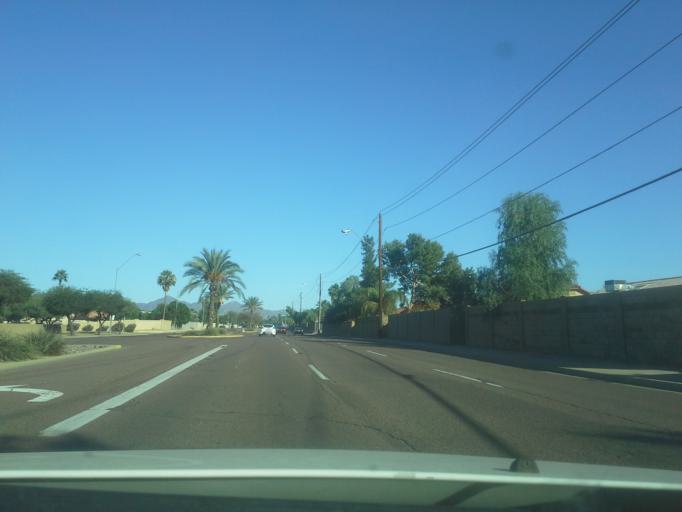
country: US
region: Arizona
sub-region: Maricopa County
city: Paradise Valley
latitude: 33.6263
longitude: -111.9903
